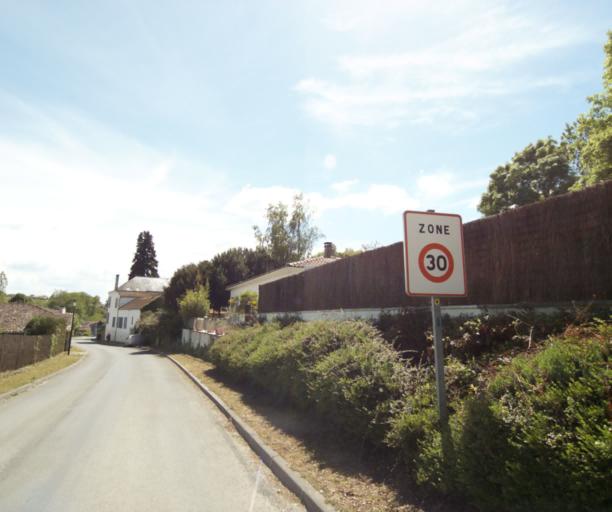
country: FR
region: Poitou-Charentes
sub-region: Departement de la Charente-Maritime
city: Chaniers
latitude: 45.7406
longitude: -0.5080
